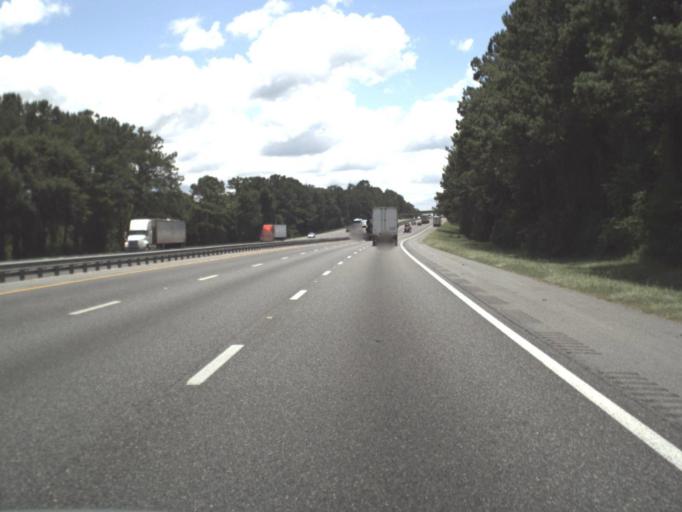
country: US
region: Florida
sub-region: Columbia County
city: Lake City
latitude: 30.0767
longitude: -82.6324
